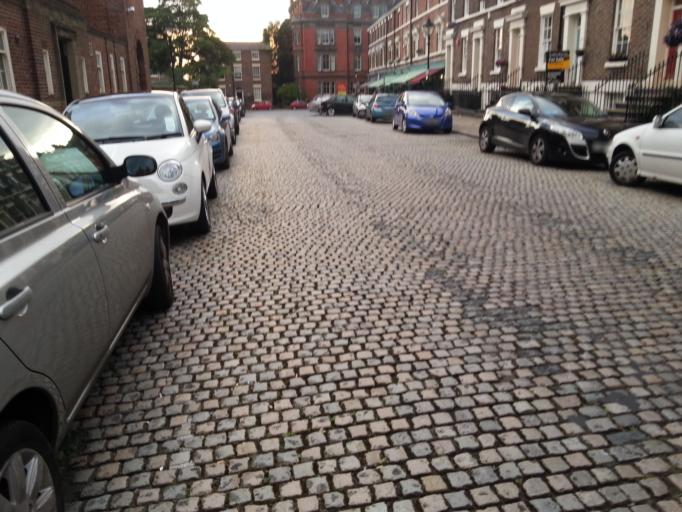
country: GB
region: England
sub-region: Liverpool
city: Liverpool
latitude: 53.4000
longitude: -2.9699
